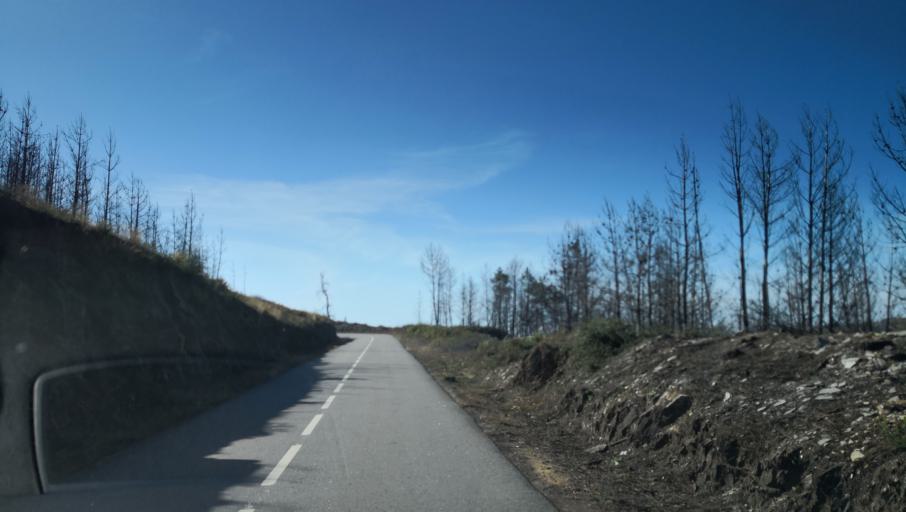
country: PT
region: Vila Real
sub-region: Sabrosa
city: Vilela
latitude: 41.2370
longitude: -7.6403
